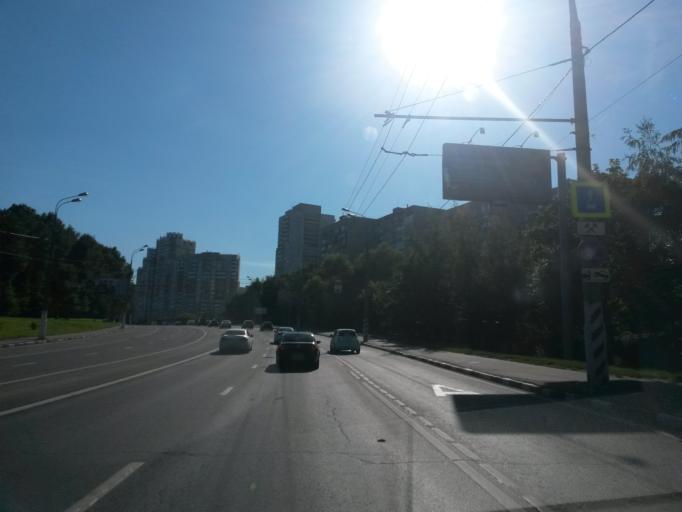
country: RU
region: Moscow
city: Zyuzino
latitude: 55.6400
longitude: 37.5470
